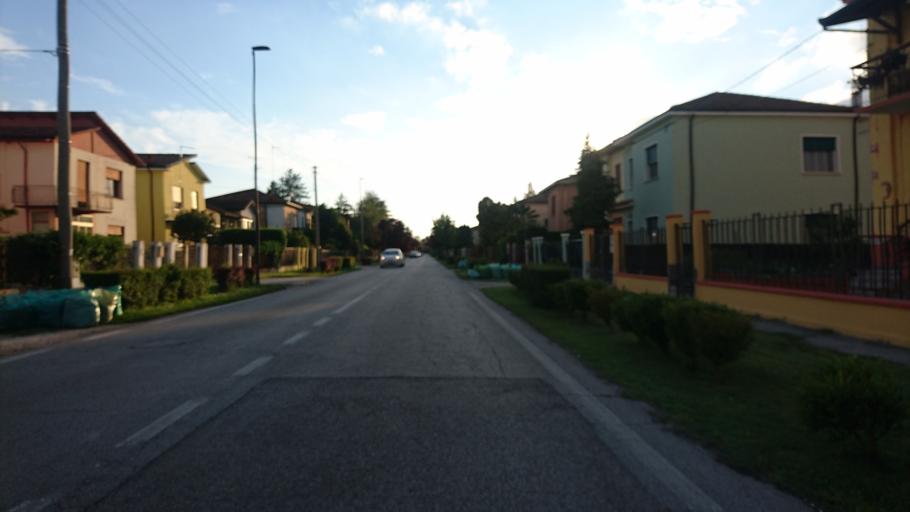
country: IT
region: Veneto
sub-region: Provincia di Rovigo
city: Castelmassa
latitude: 45.0192
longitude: 11.3155
